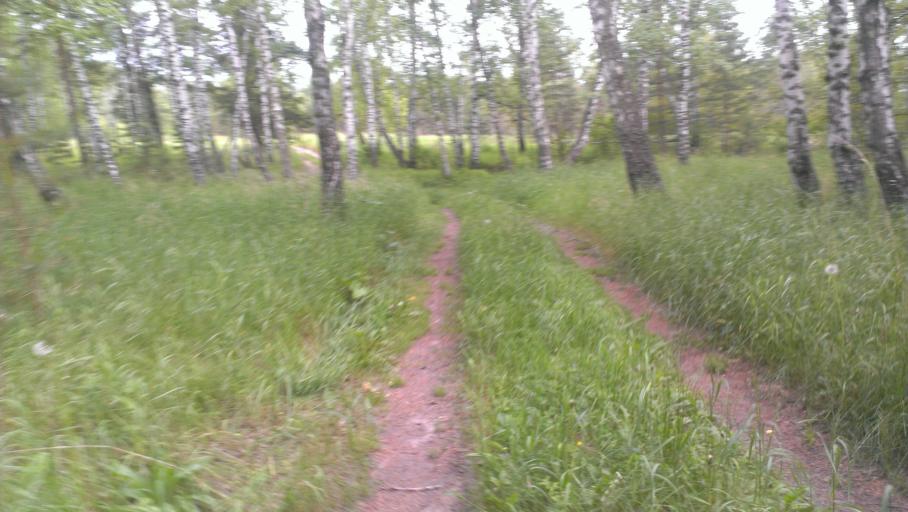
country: RU
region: Altai Krai
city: Sannikovo
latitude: 53.3382
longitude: 84.0508
